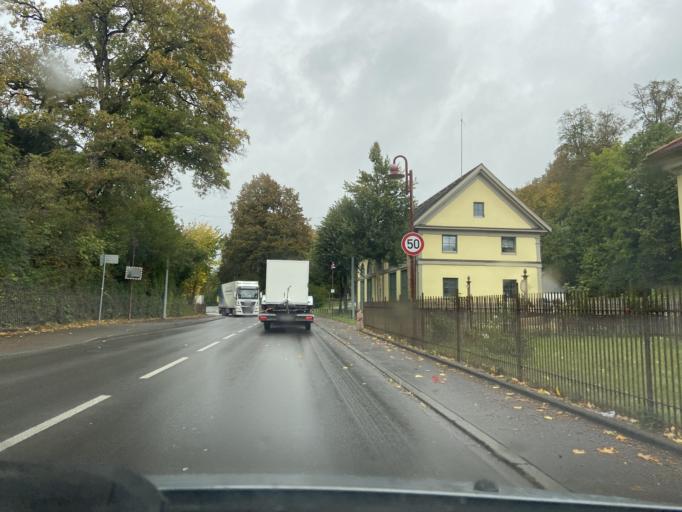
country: DE
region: Baden-Wuerttemberg
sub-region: Tuebingen Region
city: Krauchenwies
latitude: 48.0197
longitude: 9.2494
